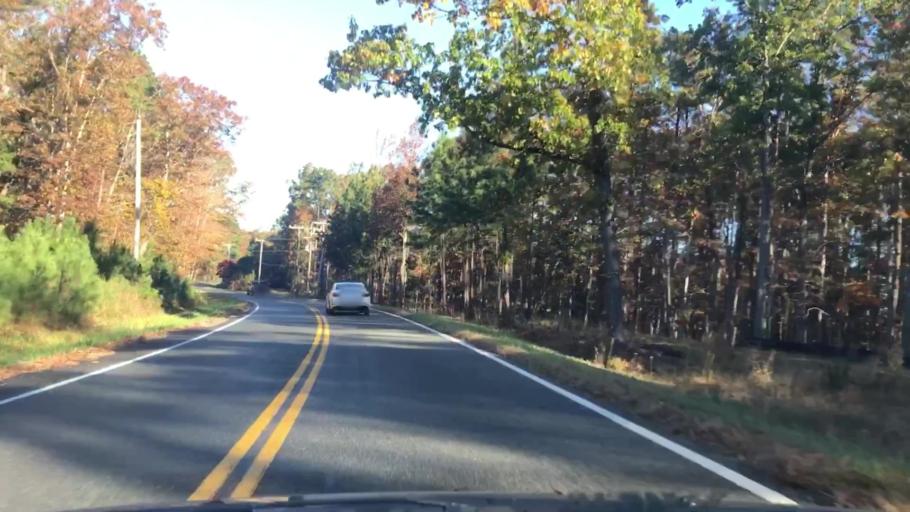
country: US
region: Virginia
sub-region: Henrico County
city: Short Pump
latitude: 37.6407
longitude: -77.6786
